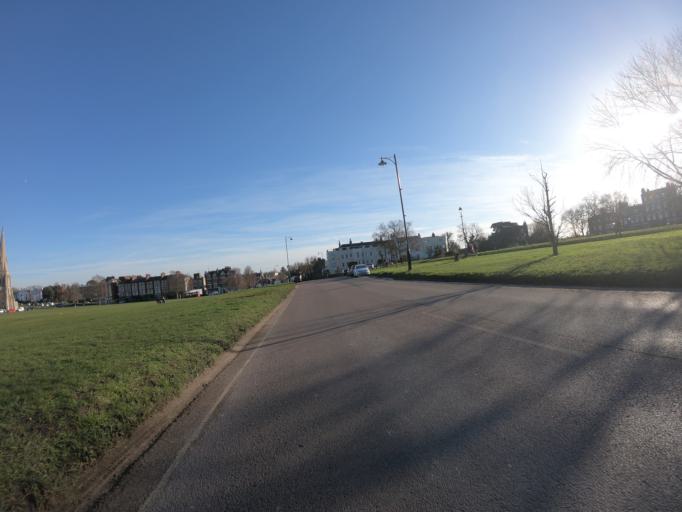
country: GB
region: England
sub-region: Greater London
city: Blackheath
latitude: 51.4681
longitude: 0.0050
